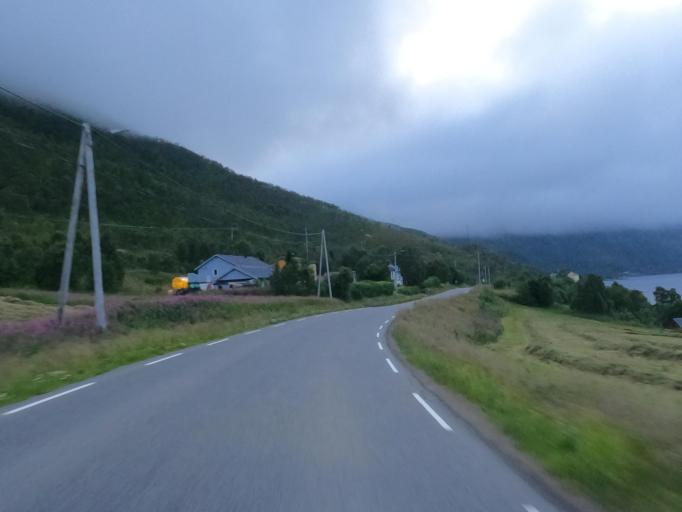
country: NO
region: Nordland
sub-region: Lodingen
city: Lodingen
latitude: 68.6048
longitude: 15.7798
